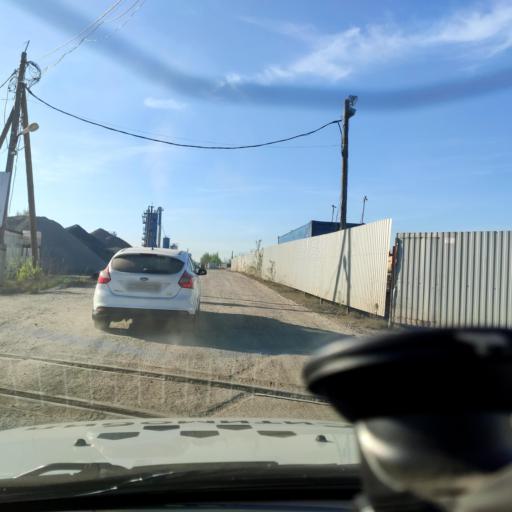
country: RU
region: Perm
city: Gamovo
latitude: 57.9073
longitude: 56.1775
